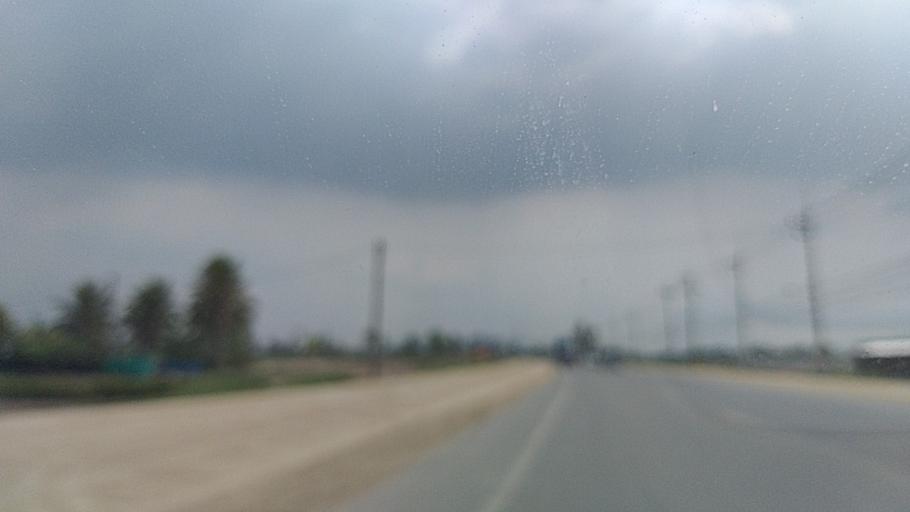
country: TH
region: Chon Buri
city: Ban Bueng
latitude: 13.3376
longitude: 101.1894
